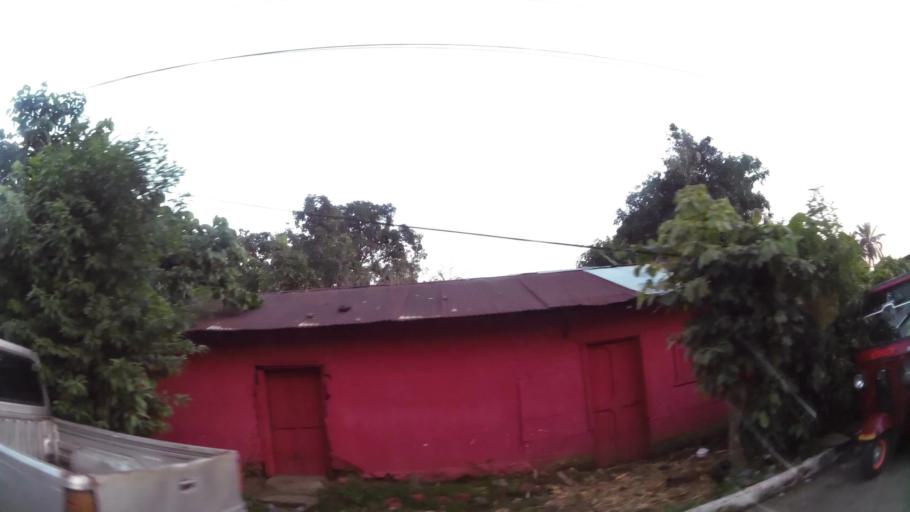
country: GT
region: Retalhuleu
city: Santa Cruz Mulua
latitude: 14.5808
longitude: -91.6240
